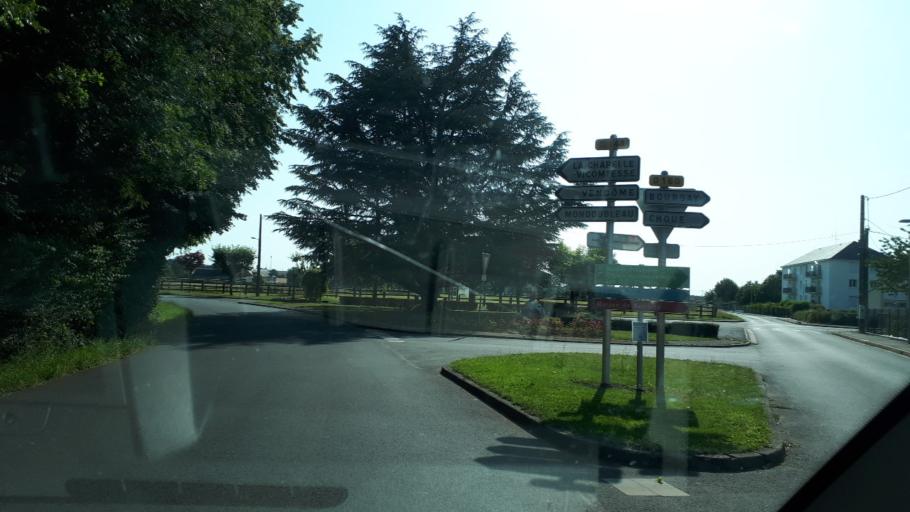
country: FR
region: Centre
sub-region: Departement du Loir-et-Cher
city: Droue
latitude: 48.0387
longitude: 1.0717
